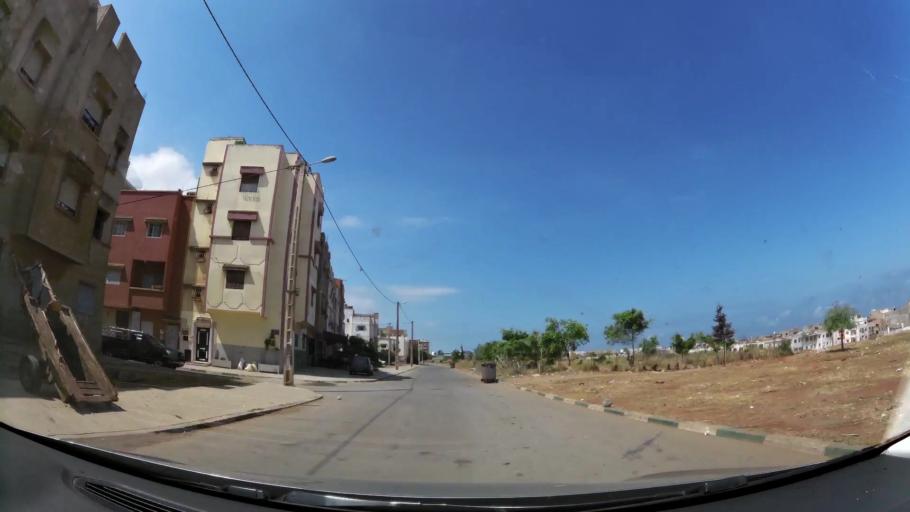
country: MA
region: Rabat-Sale-Zemmour-Zaer
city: Sale
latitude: 34.0671
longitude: -6.7826
